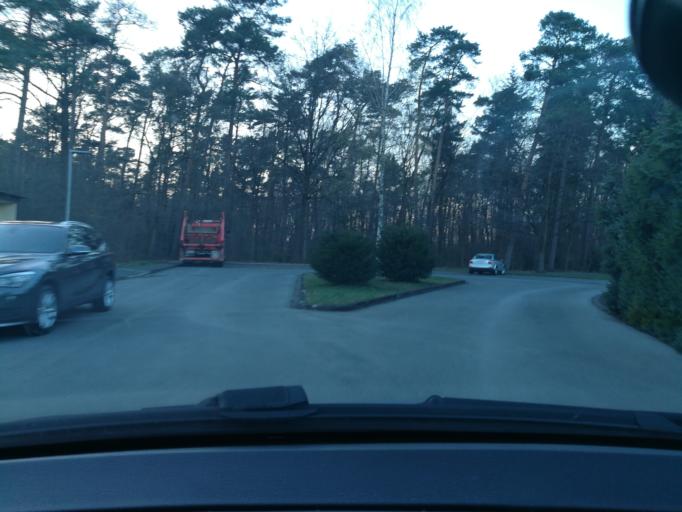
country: DE
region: North Rhine-Westphalia
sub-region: Regierungsbezirk Detmold
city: Oerlinghausen
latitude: 51.9492
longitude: 8.5901
